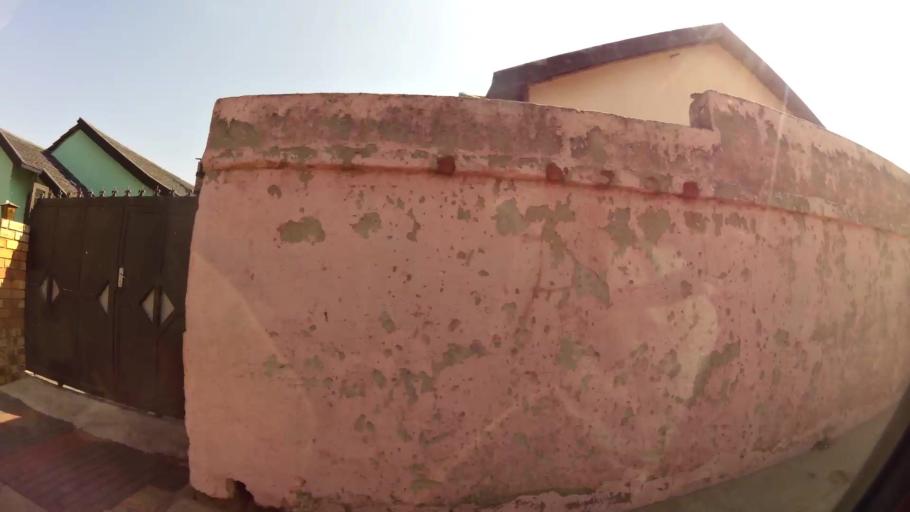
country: ZA
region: Gauteng
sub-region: City of Johannesburg Metropolitan Municipality
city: Soweto
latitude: -26.2464
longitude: 27.9401
